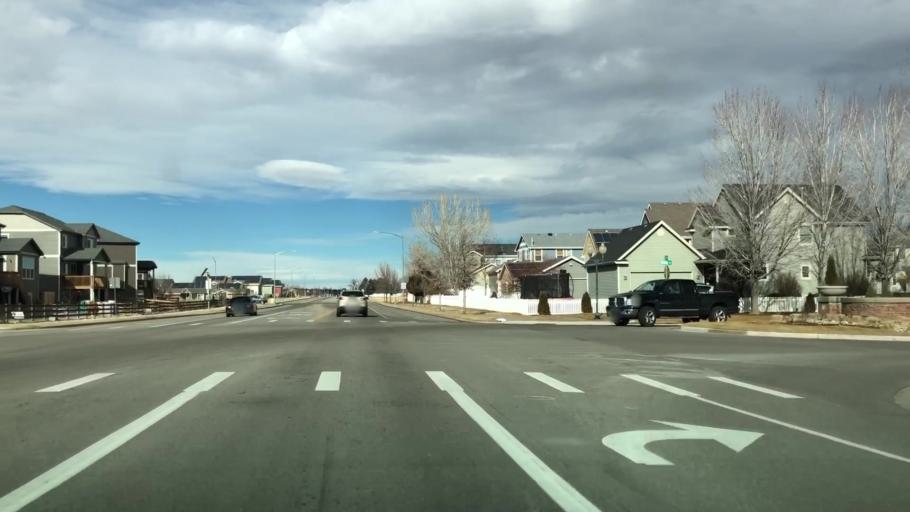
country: US
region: Colorado
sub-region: Weld County
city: Windsor
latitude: 40.4853
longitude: -104.9264
